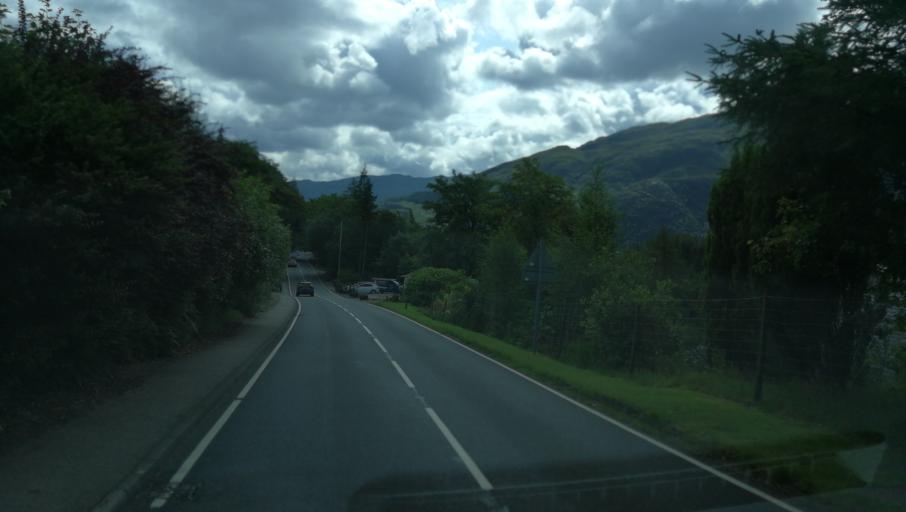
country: GB
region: Scotland
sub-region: Highland
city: Fort William
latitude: 56.8735
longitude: -5.4547
